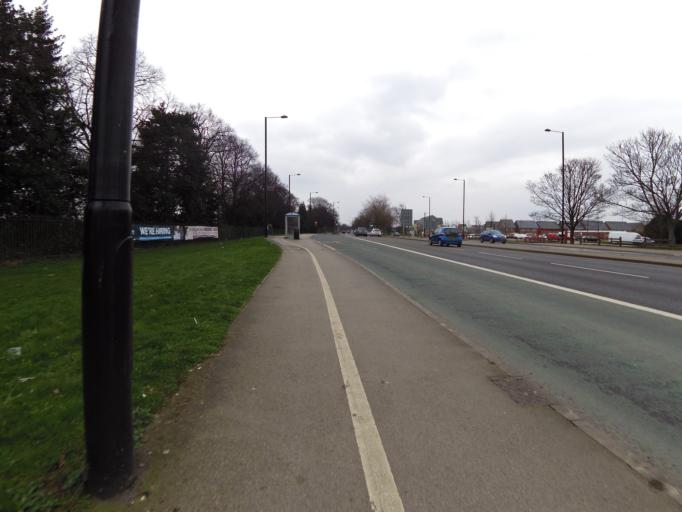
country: GB
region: England
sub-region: Doncaster
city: Doncaster
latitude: 53.5188
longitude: -1.1075
